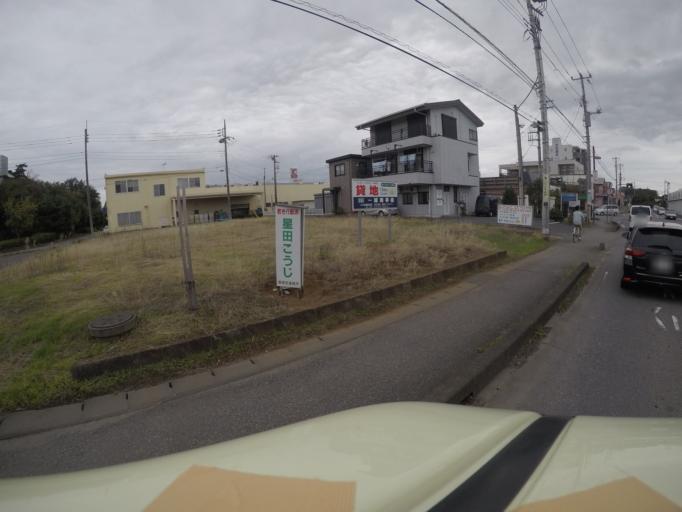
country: JP
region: Ibaraki
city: Naka
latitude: 36.1132
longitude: 140.1152
